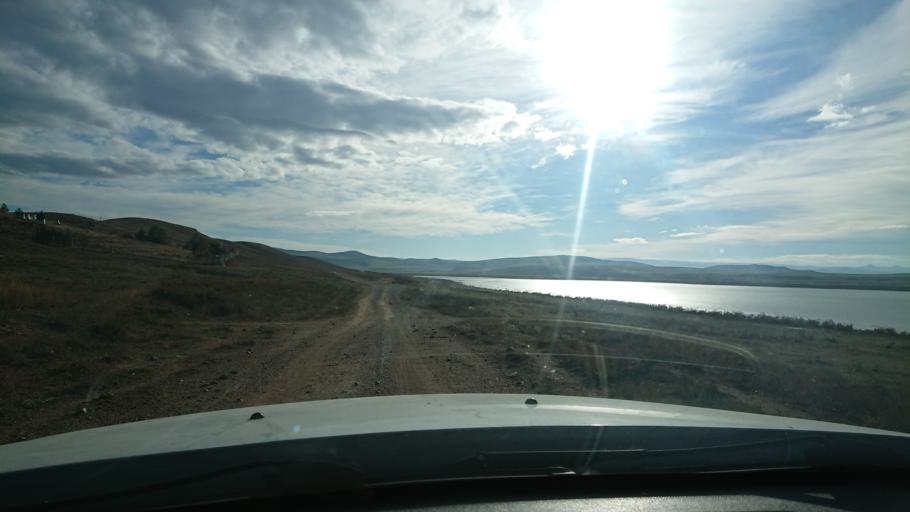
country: TR
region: Aksaray
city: Sariyahsi
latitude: 39.0509
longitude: 33.9746
